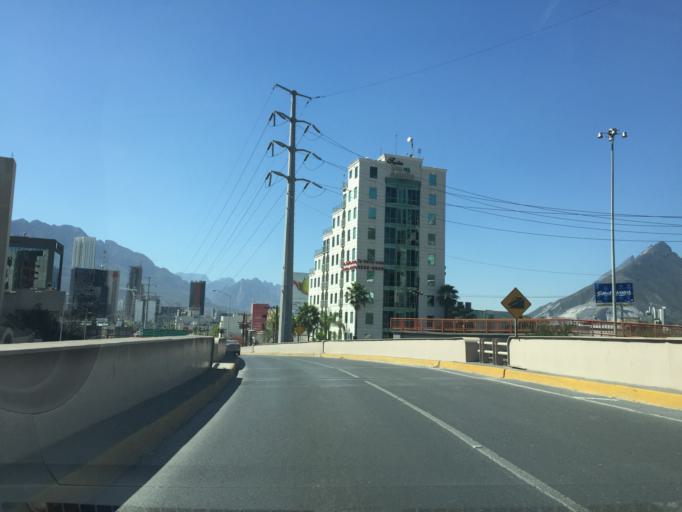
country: MX
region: Nuevo Leon
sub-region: Monterrey
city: Monterrey
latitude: 25.6543
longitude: -100.3381
